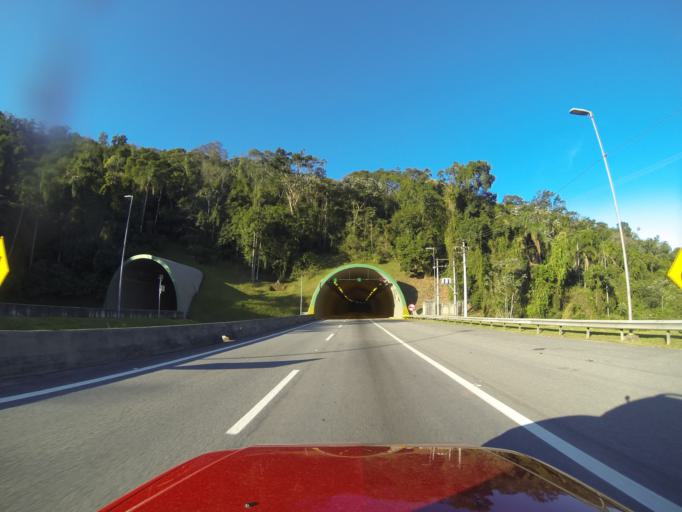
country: BR
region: Sao Paulo
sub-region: Jacarei
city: Jacarei
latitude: -23.3460
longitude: -45.9904
